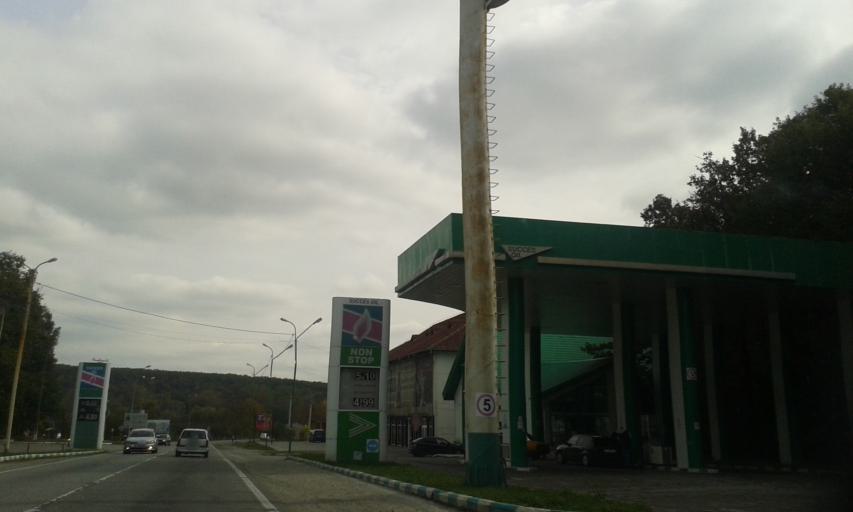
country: RO
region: Gorj
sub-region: Comuna Balanesti
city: Balanesti
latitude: 45.0396
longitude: 23.3660
